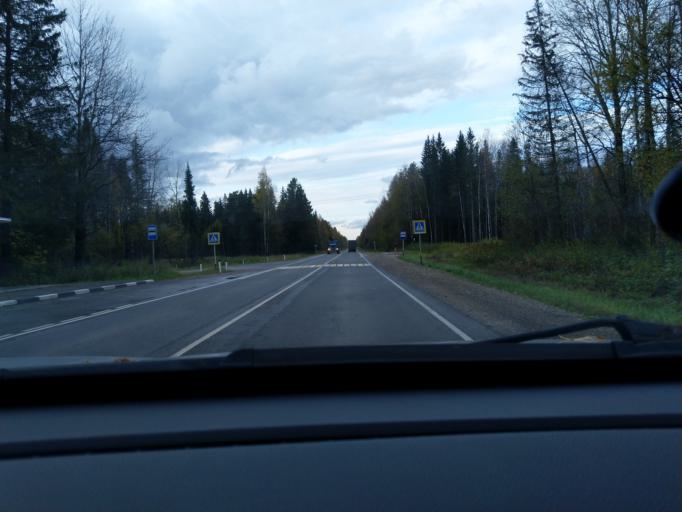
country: RU
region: Perm
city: Dobryanka
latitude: 58.3955
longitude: 56.5056
